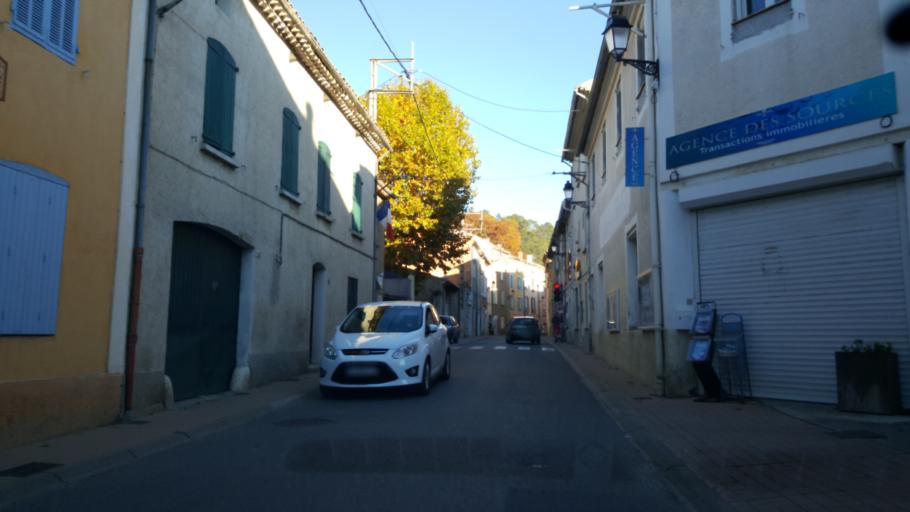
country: FR
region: Provence-Alpes-Cote d'Azur
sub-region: Departement du Var
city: Barjols
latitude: 43.5978
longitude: 5.9585
